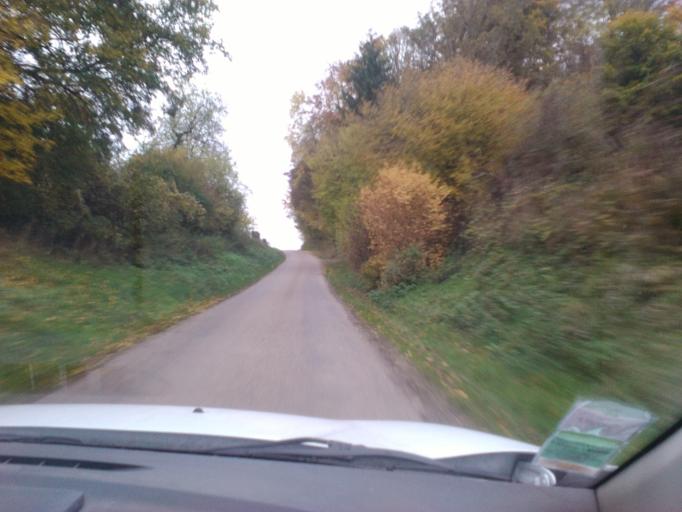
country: FR
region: Lorraine
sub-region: Departement des Vosges
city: Mirecourt
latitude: 48.3105
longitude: 6.2095
